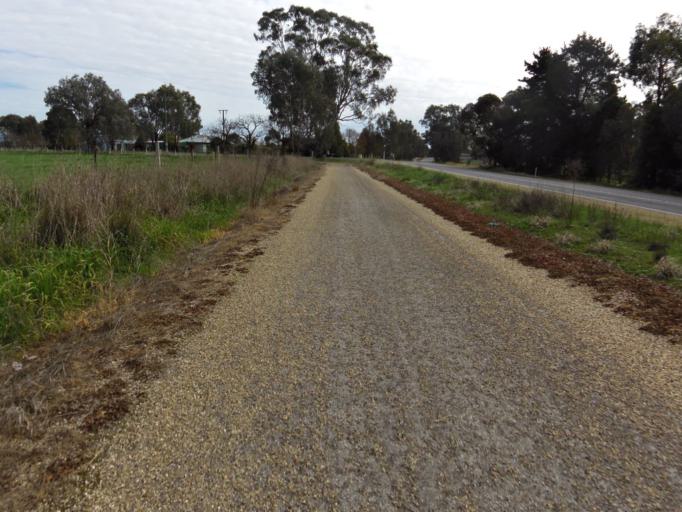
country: AU
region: Victoria
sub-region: Wangaratta
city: Wangaratta
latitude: -36.4071
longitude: 146.3496
